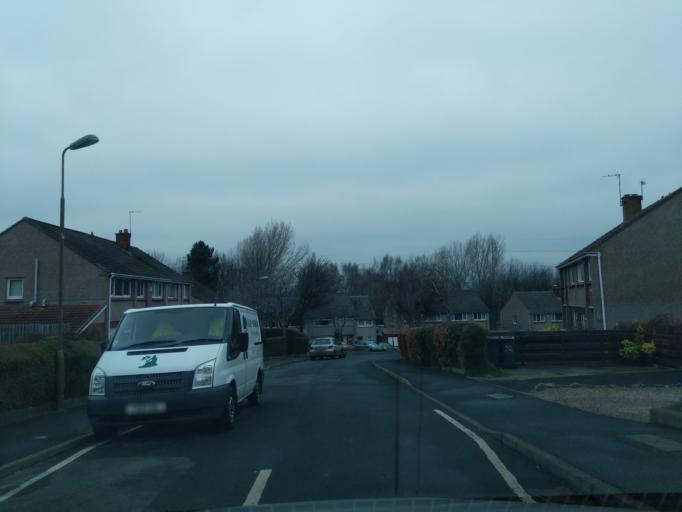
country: GB
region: Scotland
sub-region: Edinburgh
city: Currie
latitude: 55.8996
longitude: -3.3141
